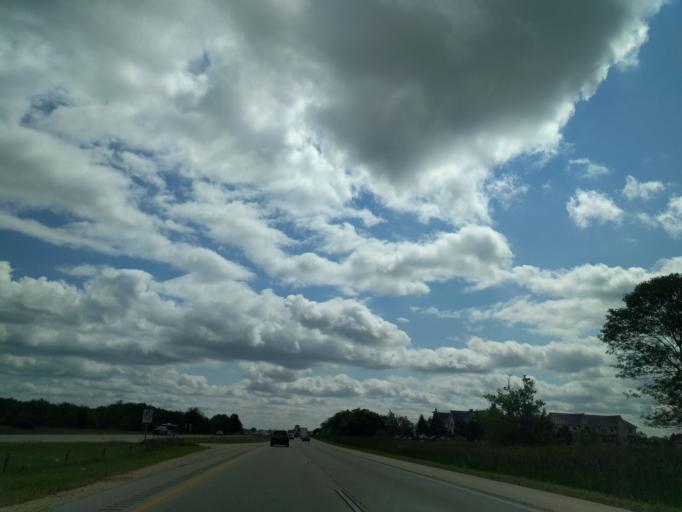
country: US
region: Wisconsin
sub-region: Milwaukee County
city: Bayside
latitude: 43.2288
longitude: -87.9205
